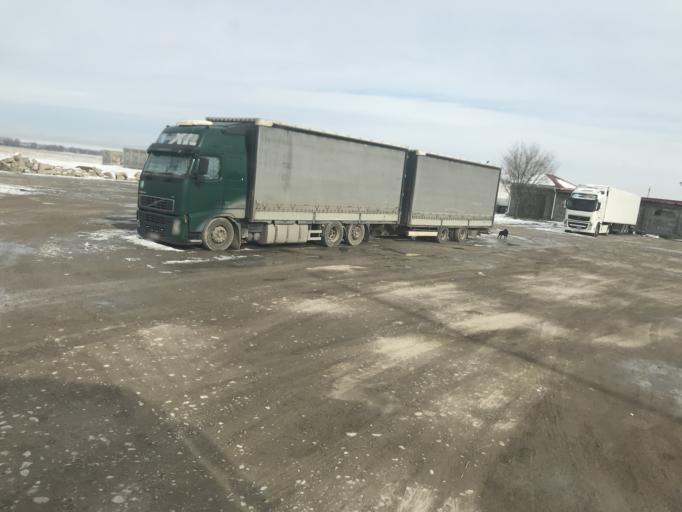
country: KZ
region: Ongtustik Qazaqstan
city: Aksu
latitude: 42.4751
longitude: 69.8187
